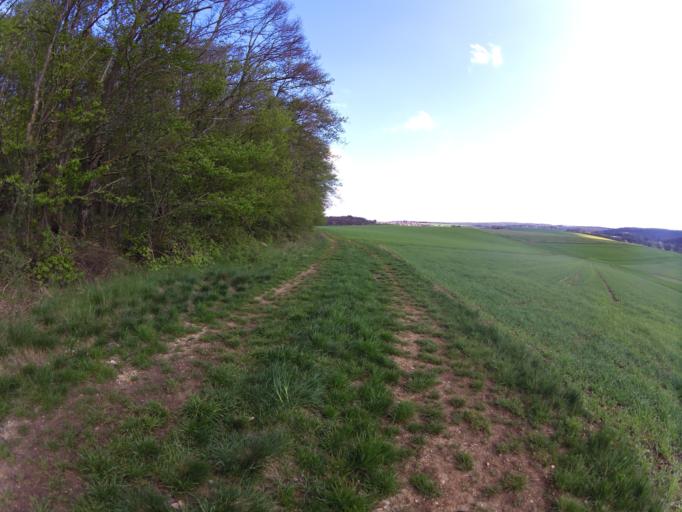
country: DE
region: Bavaria
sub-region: Regierungsbezirk Unterfranken
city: Waldbrunn
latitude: 49.7799
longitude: 9.7835
